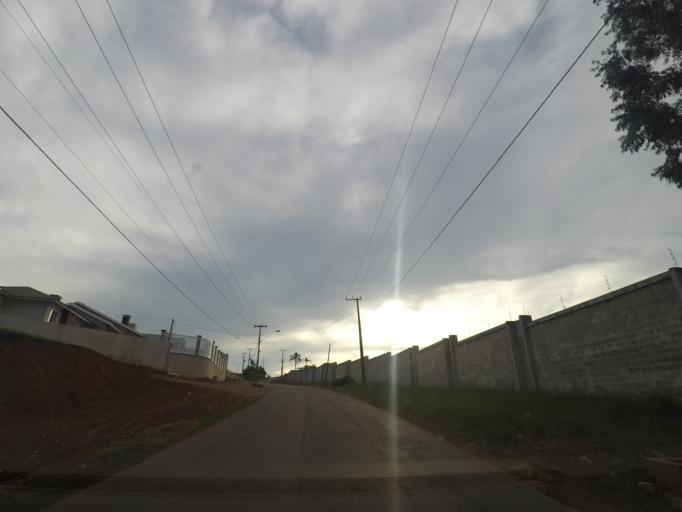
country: BR
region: Parana
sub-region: Colombo
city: Colombo
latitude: -25.2867
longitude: -49.2097
